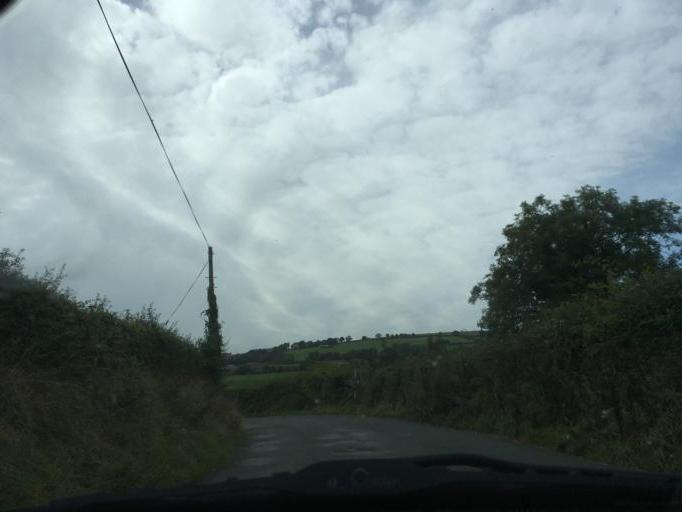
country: IE
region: Leinster
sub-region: Wicklow
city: Rathnew
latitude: 52.9239
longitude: -6.1075
